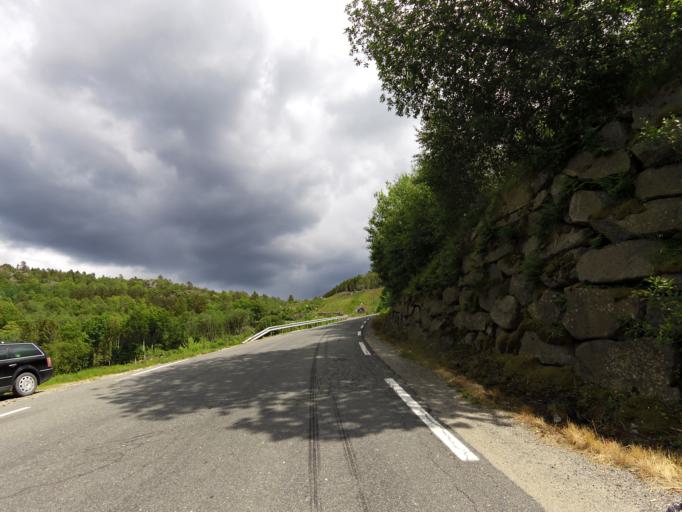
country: NO
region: Vest-Agder
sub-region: Lyngdal
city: Lyngdal
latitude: 58.1151
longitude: 7.0624
